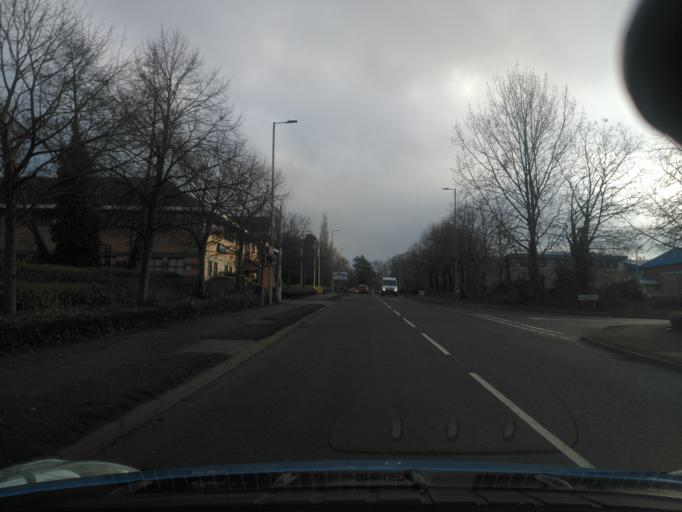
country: GB
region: England
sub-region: Hertfordshire
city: Letchworth Garden City
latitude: 51.9797
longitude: -0.2072
